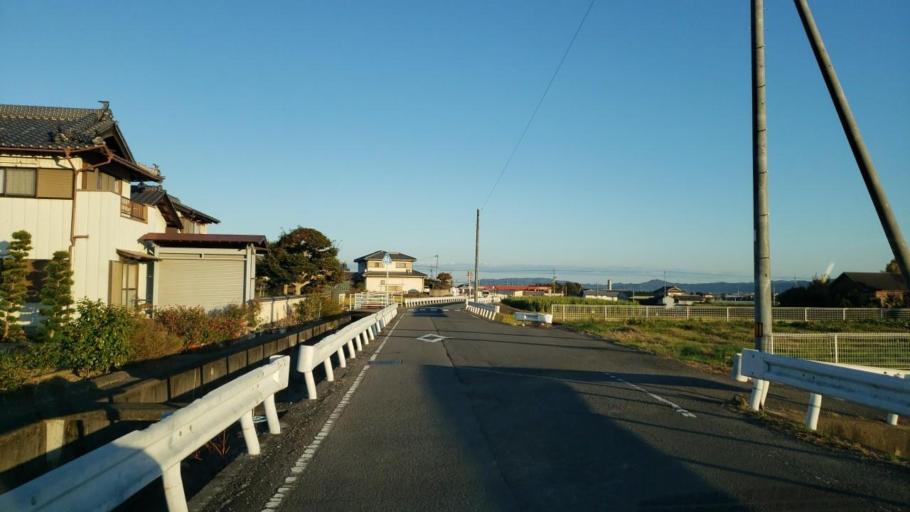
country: JP
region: Tokushima
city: Kamojimacho-jogejima
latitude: 34.1129
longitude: 134.3472
